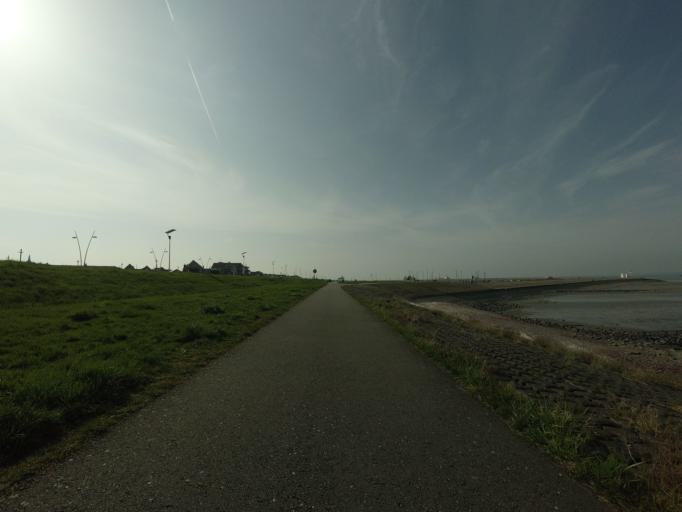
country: NL
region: Zeeland
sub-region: Gemeente Terneuzen
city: Terneuzen
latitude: 51.3389
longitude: 3.8311
